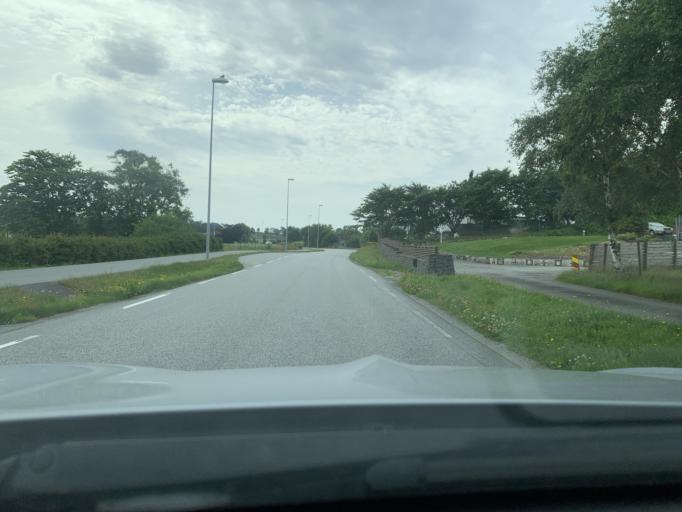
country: NO
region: Rogaland
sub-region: Time
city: Bryne
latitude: 58.7605
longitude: 5.7095
